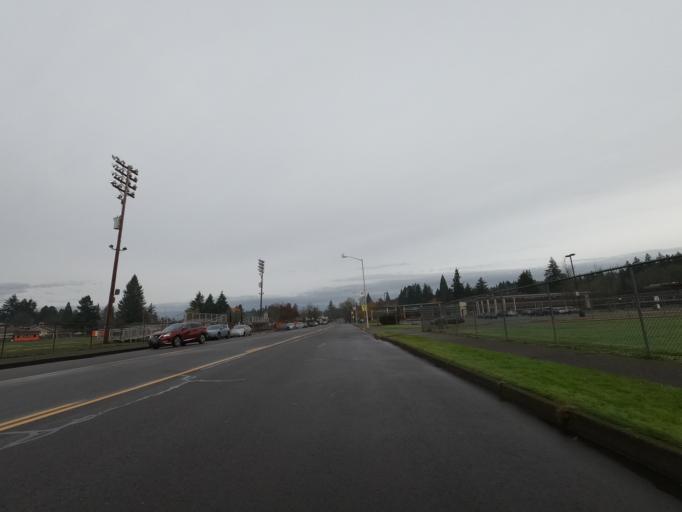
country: US
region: Oregon
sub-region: Clackamas County
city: Gladstone
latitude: 45.3857
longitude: -122.5982
